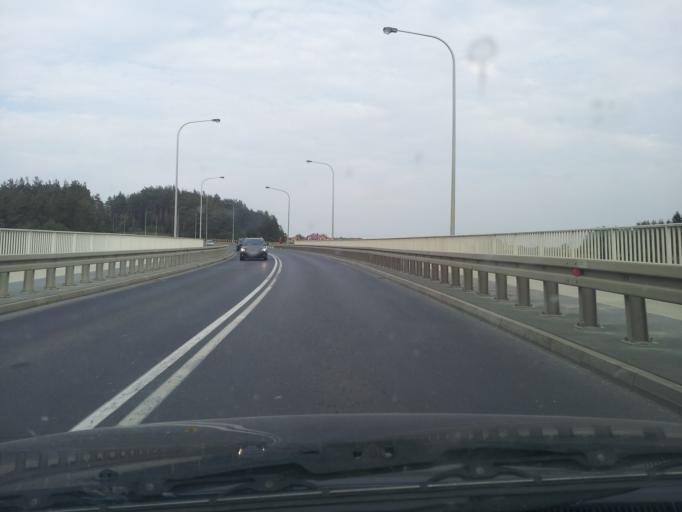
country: PL
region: Warmian-Masurian Voivodeship
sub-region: Powiat ilawski
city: Ilawa
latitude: 53.5878
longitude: 19.5846
